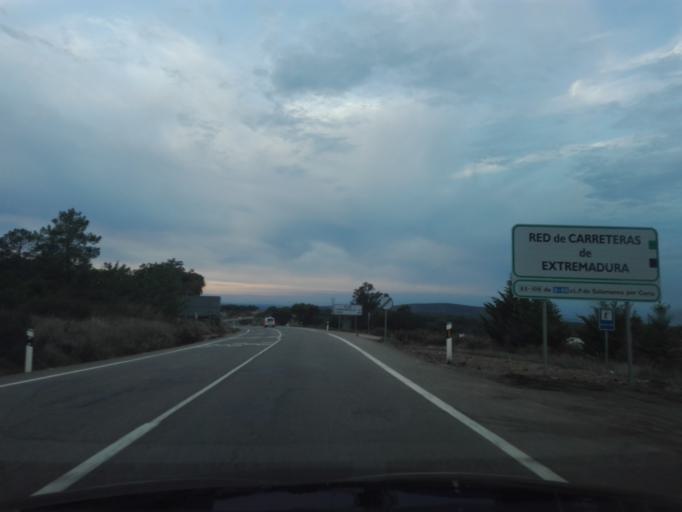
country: ES
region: Extremadura
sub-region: Provincia de Caceres
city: Casas de Millan
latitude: 39.8203
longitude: -6.3653
